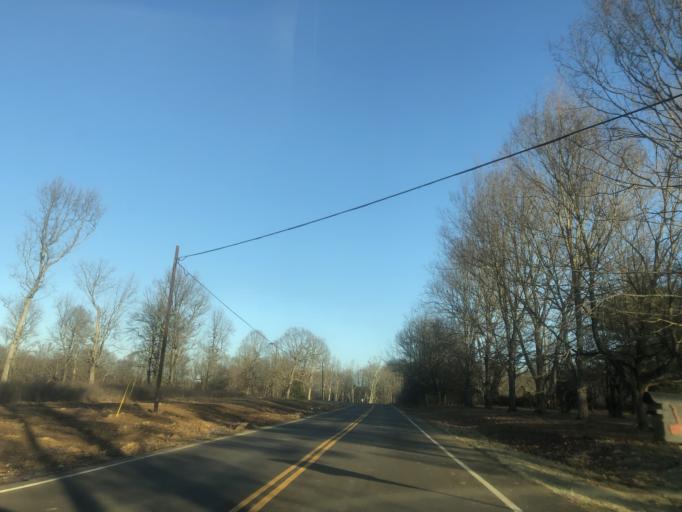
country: US
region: Tennessee
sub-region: Sumner County
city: White House
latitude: 36.4813
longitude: -86.7012
